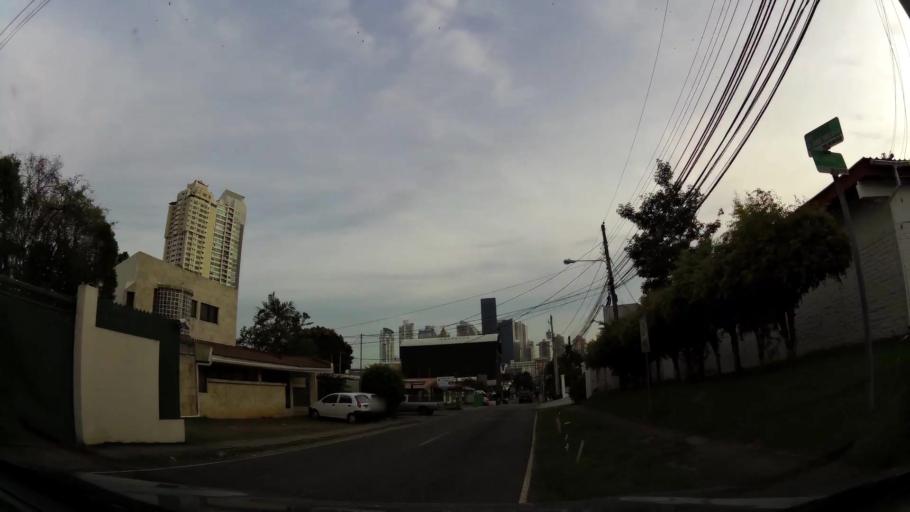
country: PA
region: Panama
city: Panama
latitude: 8.9902
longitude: -79.5133
